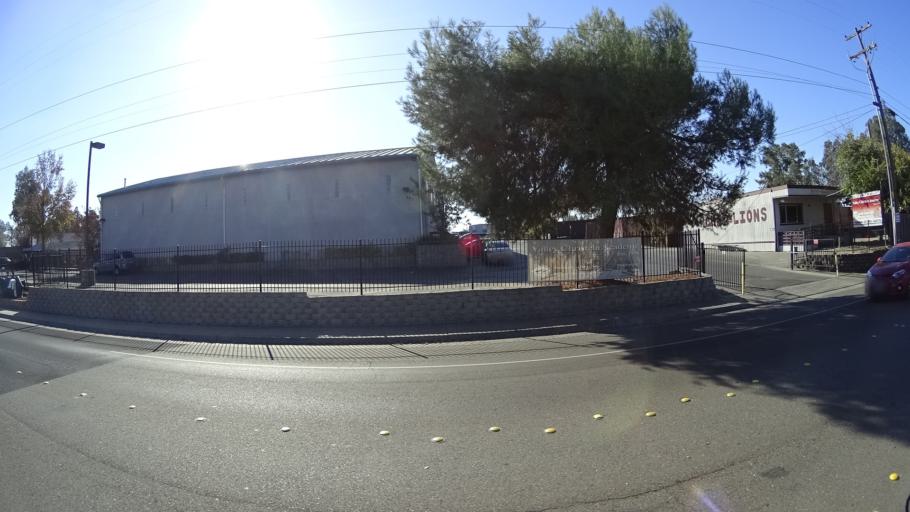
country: US
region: California
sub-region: Sacramento County
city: Citrus Heights
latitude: 38.7221
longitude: -121.2955
